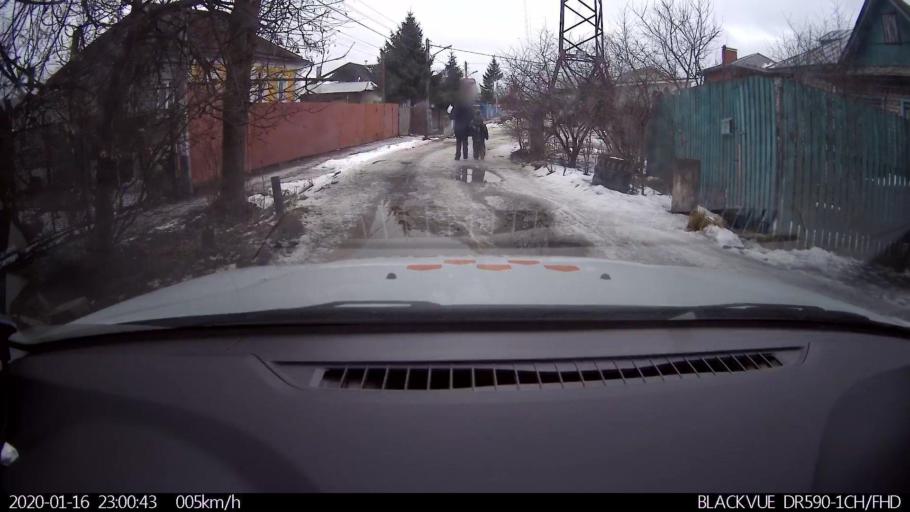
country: RU
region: Nizjnij Novgorod
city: Nizhniy Novgorod
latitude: 56.2856
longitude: 43.9055
